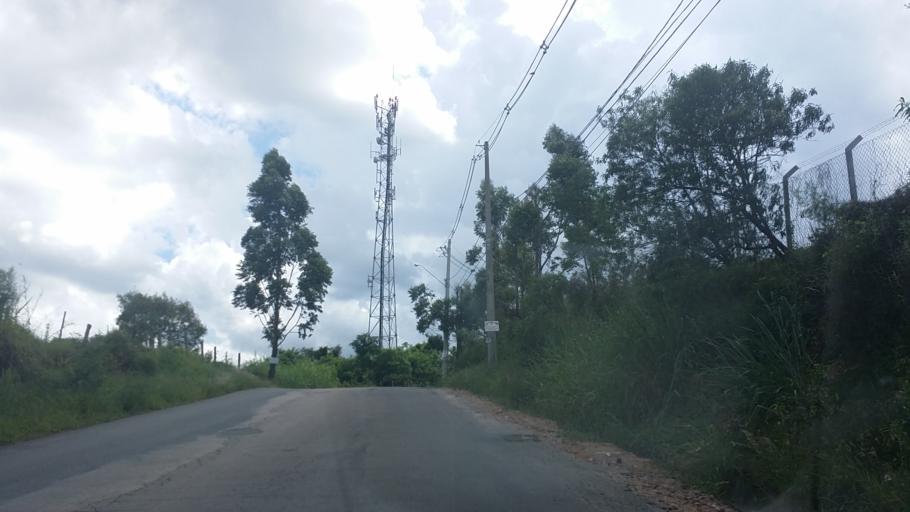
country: BR
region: Sao Paulo
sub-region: Itupeva
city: Itupeva
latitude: -23.1642
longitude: -47.0738
